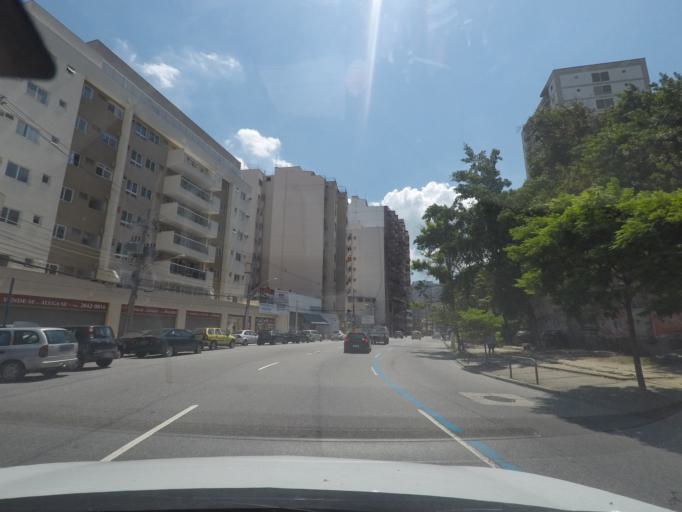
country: BR
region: Rio de Janeiro
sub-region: Rio De Janeiro
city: Rio de Janeiro
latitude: -22.9167
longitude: -43.2545
